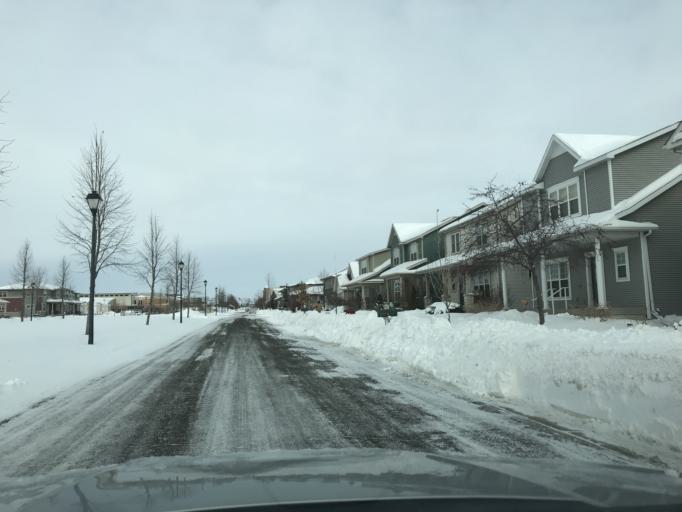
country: US
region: Wisconsin
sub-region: Dane County
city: Sun Prairie
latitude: 43.1586
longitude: -89.2618
